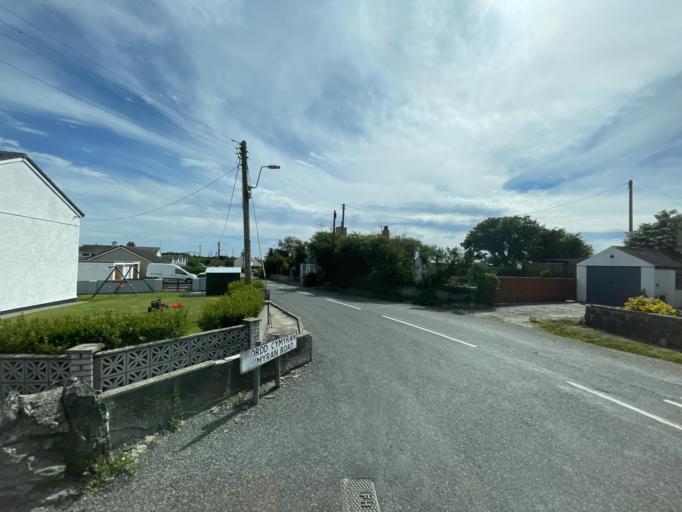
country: GB
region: Wales
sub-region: Anglesey
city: Valley
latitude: 53.2770
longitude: -4.5436
